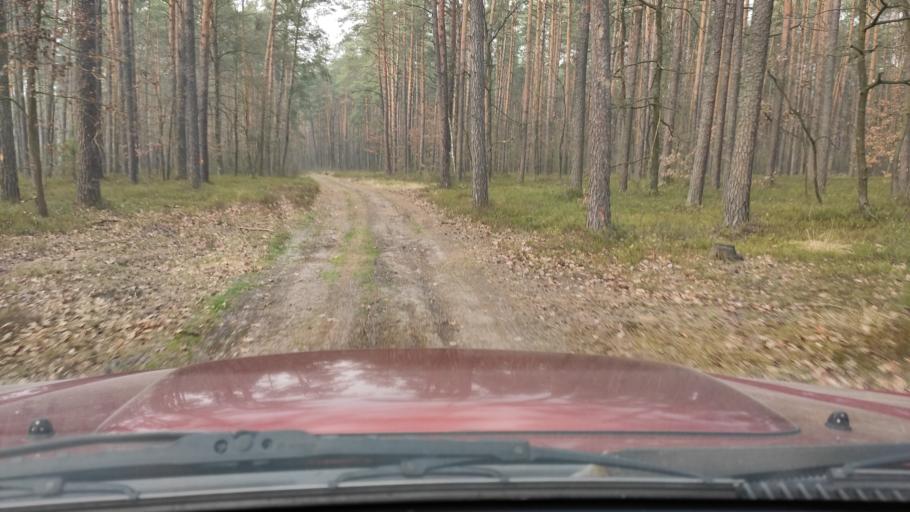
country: PL
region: Masovian Voivodeship
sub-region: Powiat zwolenski
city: Zwolen
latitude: 51.3962
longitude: 21.5706
